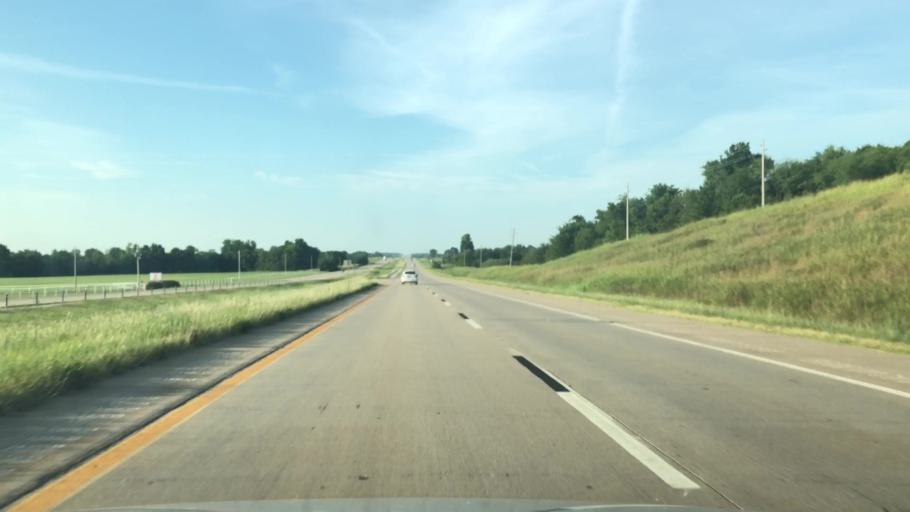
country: US
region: Oklahoma
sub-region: Tulsa County
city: Collinsville
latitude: 36.4763
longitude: -95.9170
